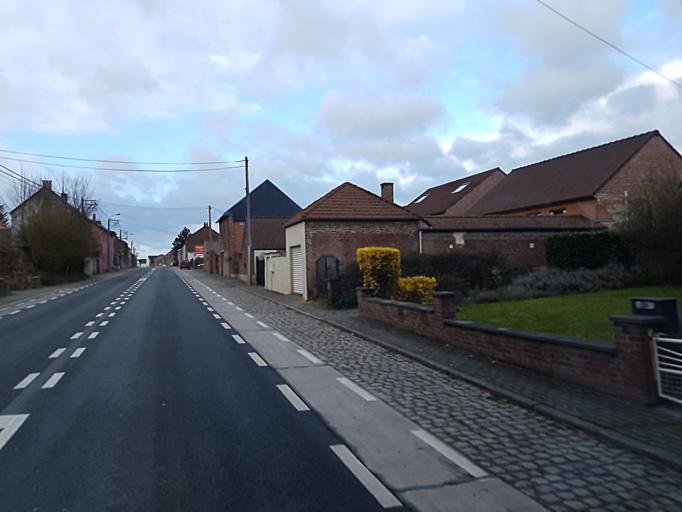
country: BE
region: Flanders
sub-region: Provincie Vlaams-Brabant
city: Hoegaarden
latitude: 50.7562
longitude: 4.8832
